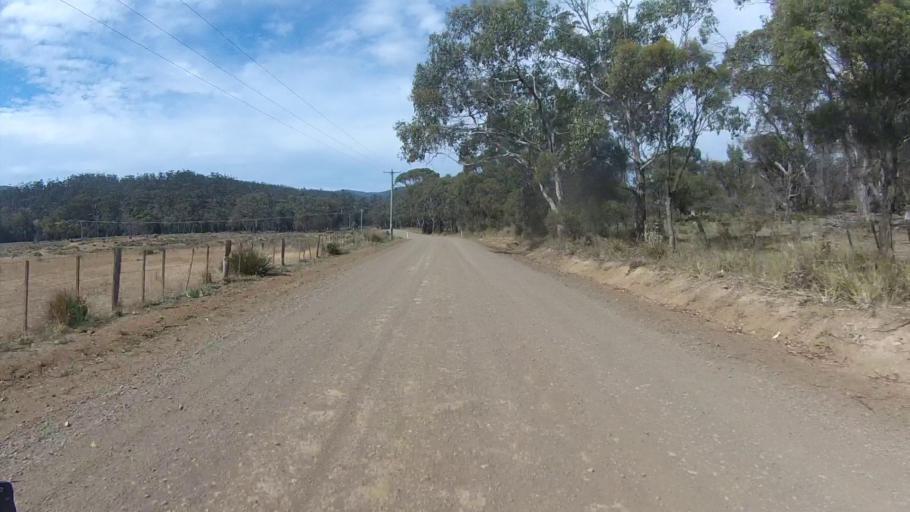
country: AU
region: Tasmania
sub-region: Sorell
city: Sorell
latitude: -42.6451
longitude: 147.9000
